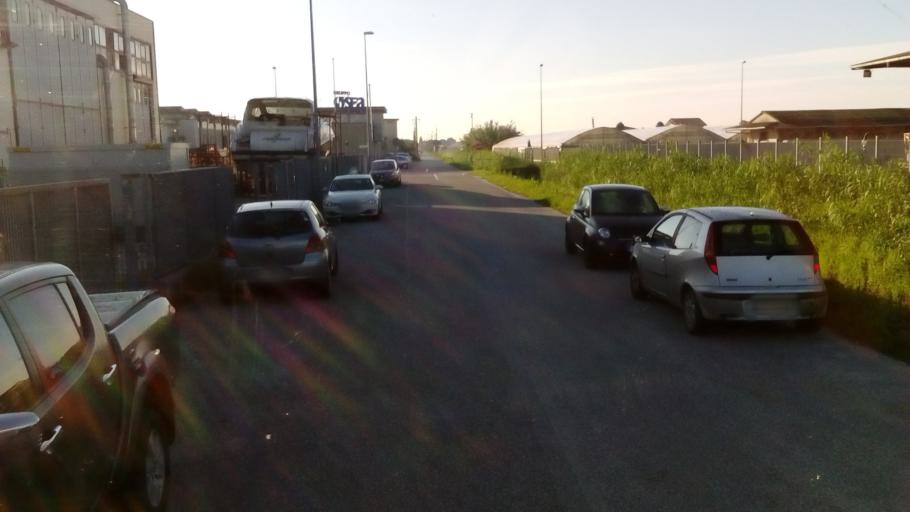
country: IT
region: Tuscany
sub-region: Provincia di Lucca
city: Viareggio
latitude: 43.8582
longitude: 10.2768
